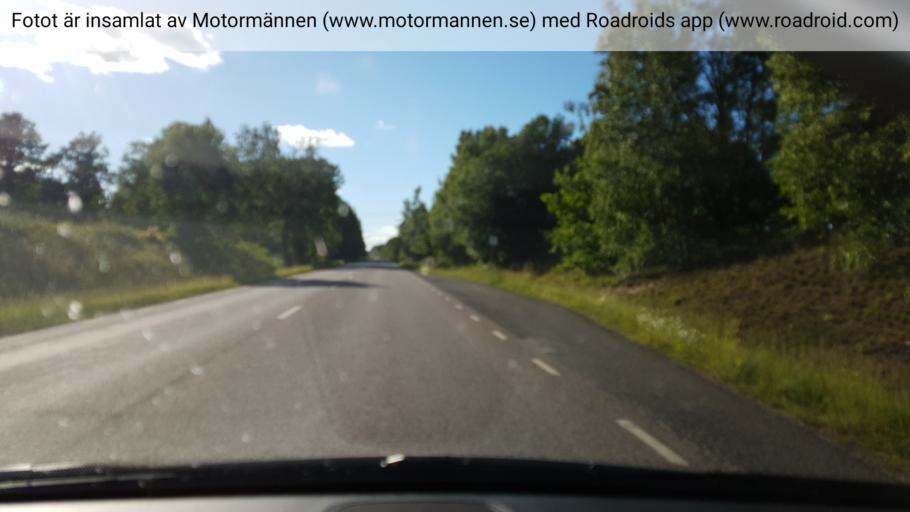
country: SE
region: Vaestra Goetaland
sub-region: Tidaholms Kommun
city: Olofstorp
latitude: 58.3586
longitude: 14.0383
